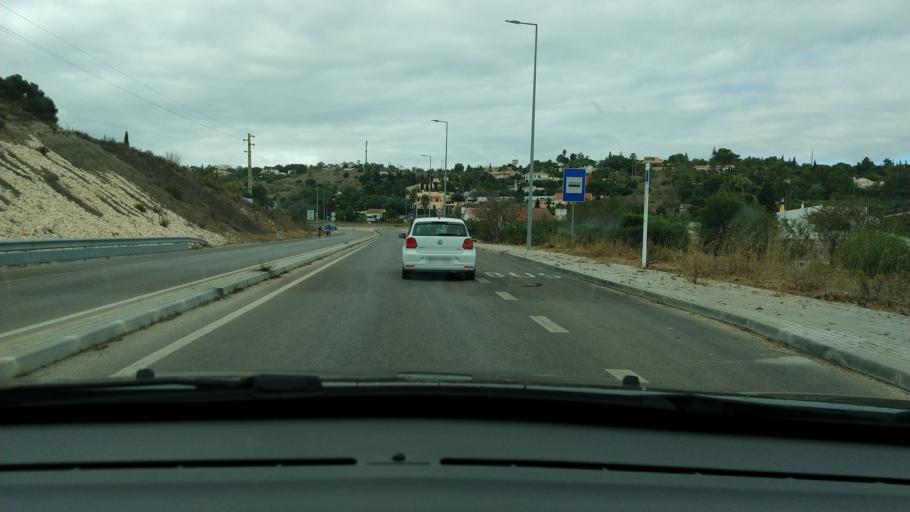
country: PT
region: Faro
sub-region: Lagos
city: Lagos
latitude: 37.1060
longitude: -8.7052
